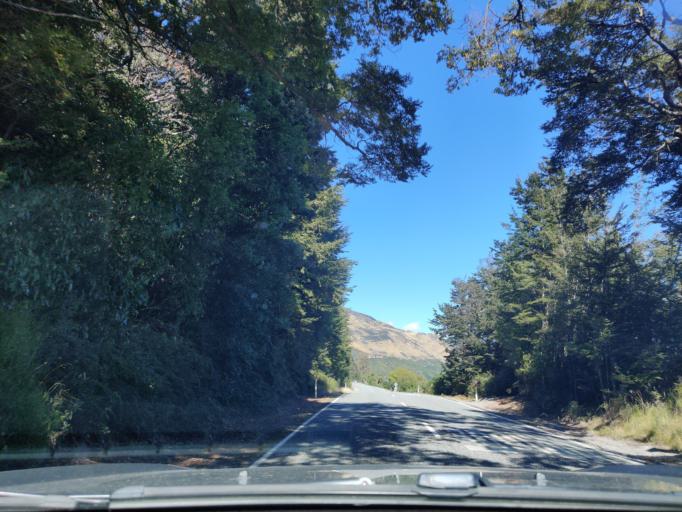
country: NZ
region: Otago
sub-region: Queenstown-Lakes District
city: Queenstown
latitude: -44.9930
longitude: 168.4325
